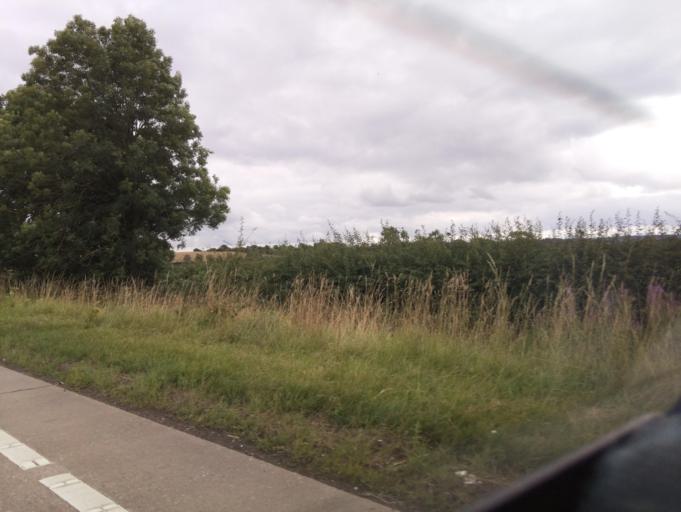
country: GB
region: England
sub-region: Lincolnshire
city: Long Bennington
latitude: 52.9335
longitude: -0.8095
